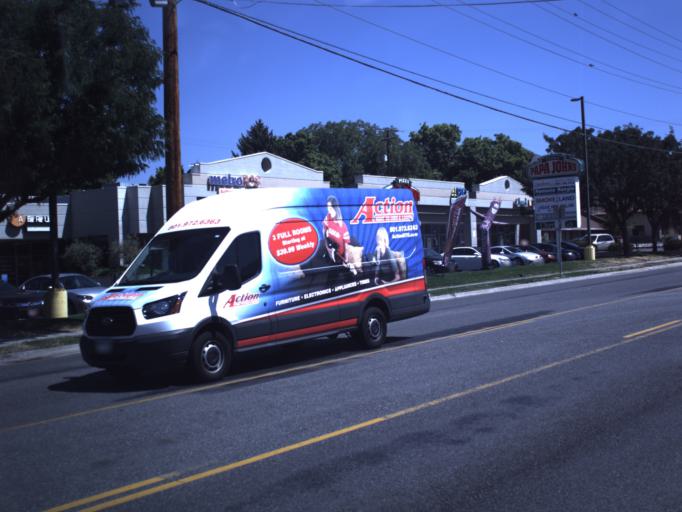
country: US
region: Utah
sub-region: Salt Lake County
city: Millcreek
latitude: 40.6998
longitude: -111.8701
